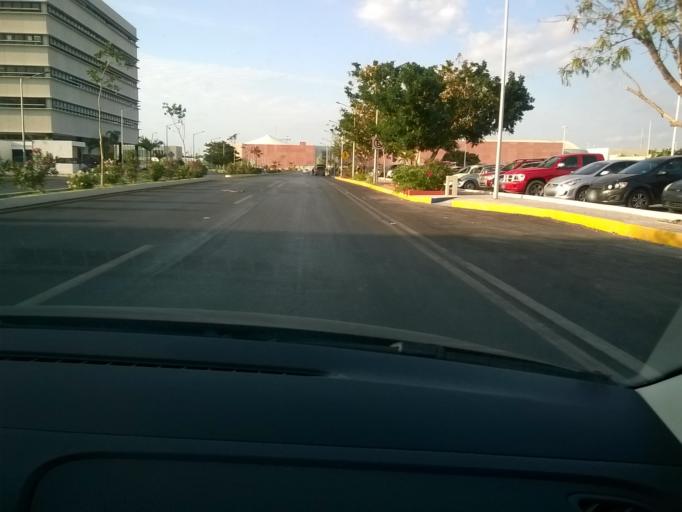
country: MX
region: Yucatan
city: Merida
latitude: 21.0351
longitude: -89.6319
